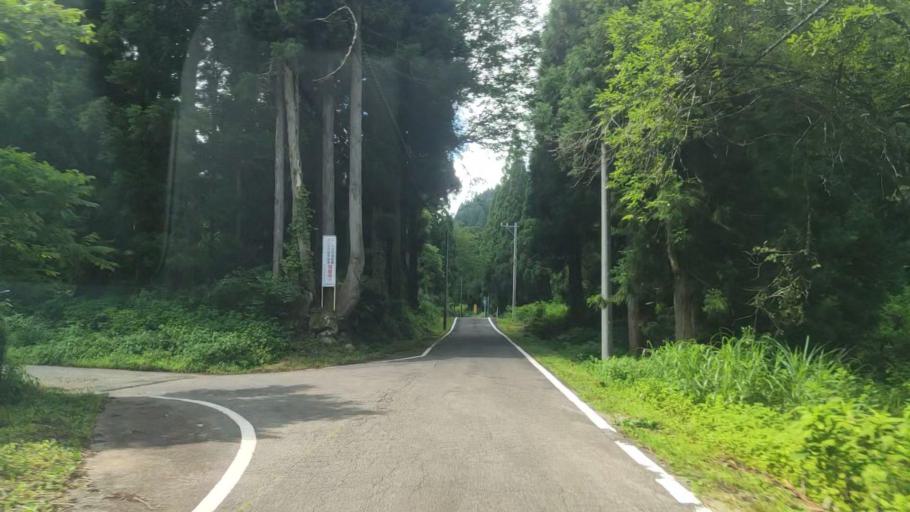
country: JP
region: Fukui
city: Katsuyama
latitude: 36.2044
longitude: 136.5256
